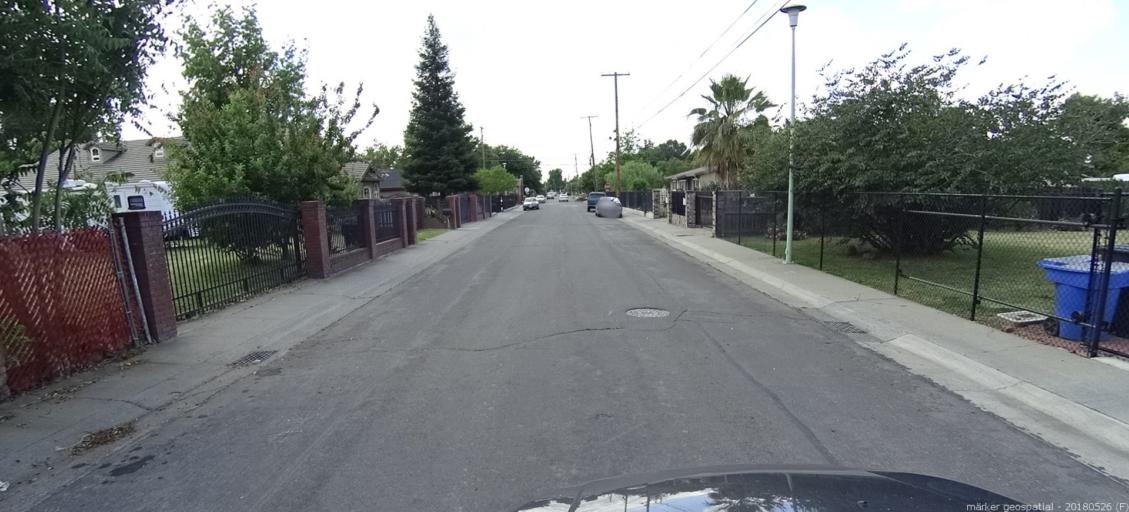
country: US
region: California
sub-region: Sacramento County
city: Sacramento
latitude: 38.6157
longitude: -121.4707
